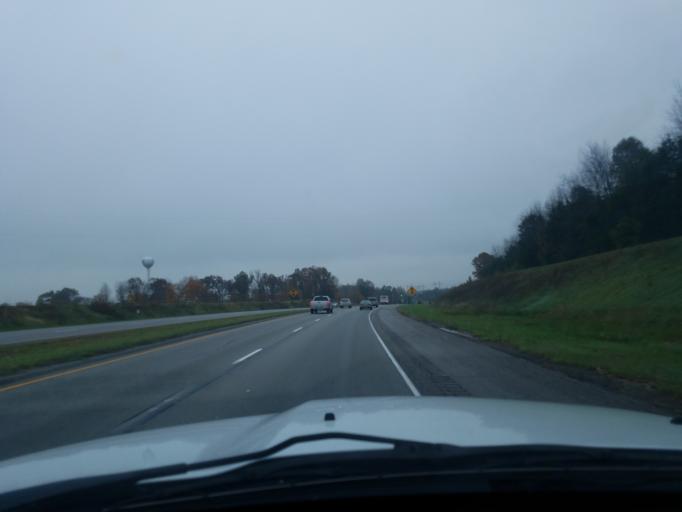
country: US
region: Kentucky
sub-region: Hardin County
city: Elizabethtown
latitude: 37.6681
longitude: -85.8425
